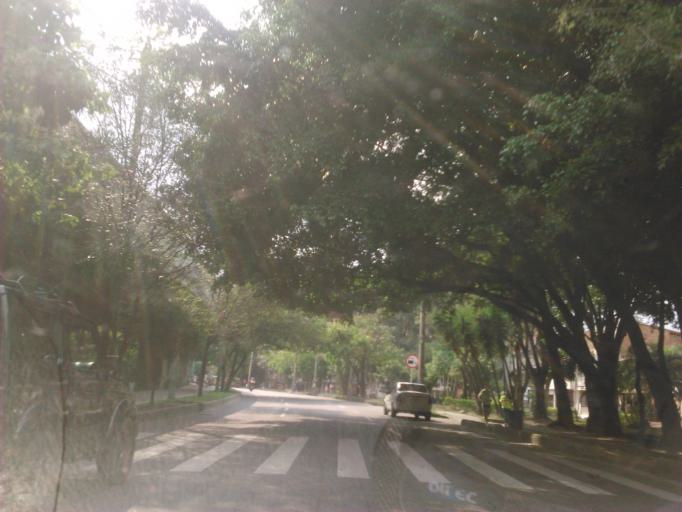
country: CO
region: Antioquia
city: Medellin
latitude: 6.2577
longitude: -75.5935
